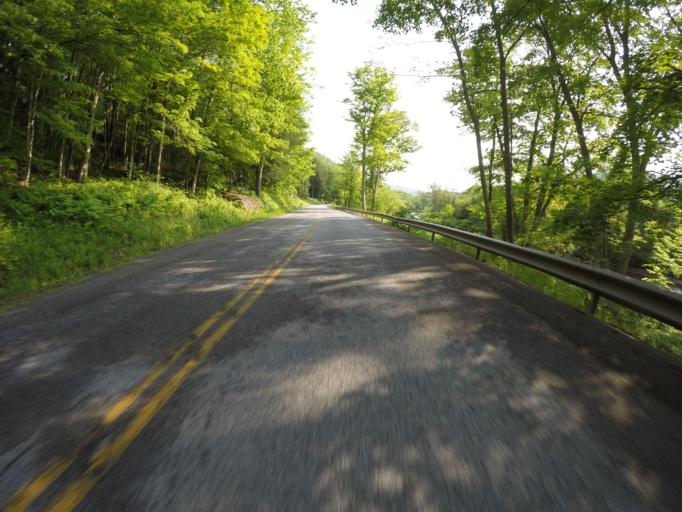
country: US
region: New York
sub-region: Delaware County
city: Stamford
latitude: 42.1324
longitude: -74.6682
